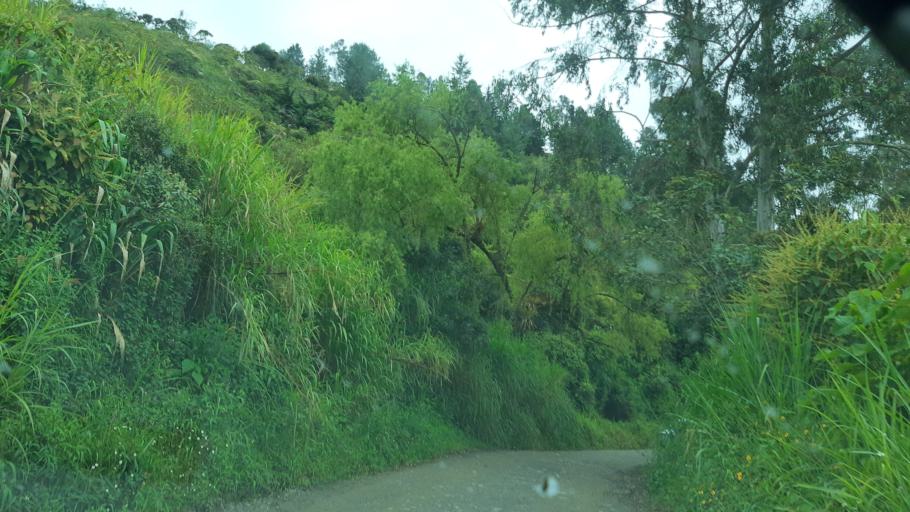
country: CO
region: Boyaca
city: Guateque
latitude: 5.0357
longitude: -73.4401
